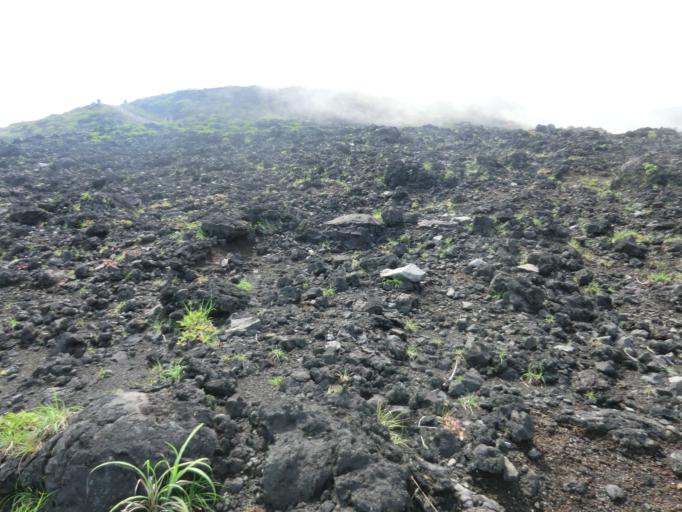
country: JP
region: Shizuoka
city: Ito
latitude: 34.7261
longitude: 139.3912
